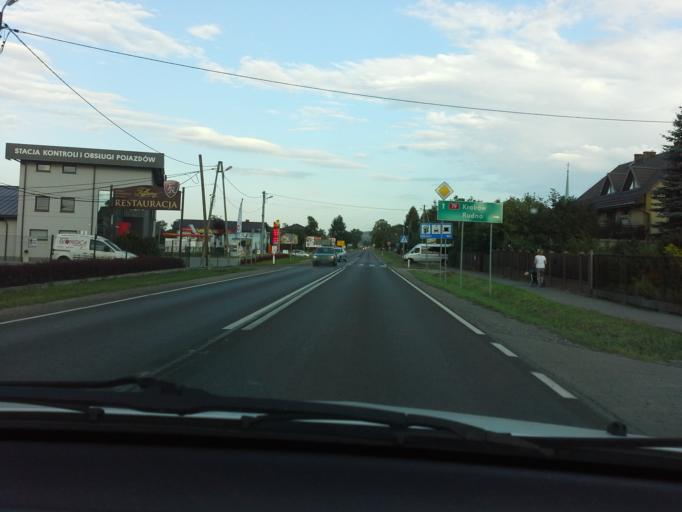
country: PL
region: Lesser Poland Voivodeship
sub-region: Powiat krakowski
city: Wola Filipowska
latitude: 50.1342
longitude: 19.5786
